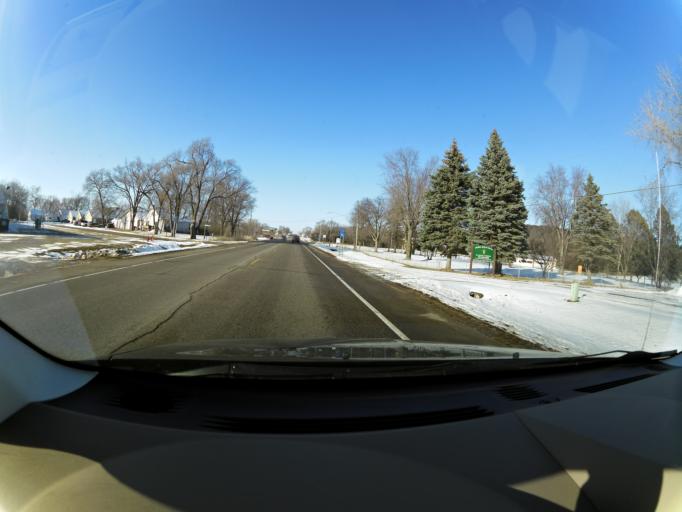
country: US
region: Minnesota
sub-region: Goodhue County
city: Cannon Falls
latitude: 44.5206
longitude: -92.9081
